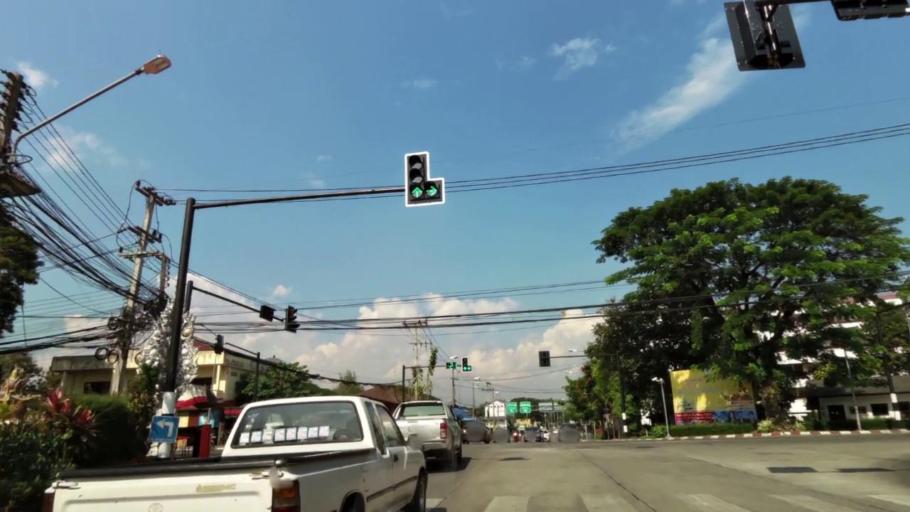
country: TH
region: Chiang Rai
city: Chiang Rai
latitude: 19.9126
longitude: 99.8325
